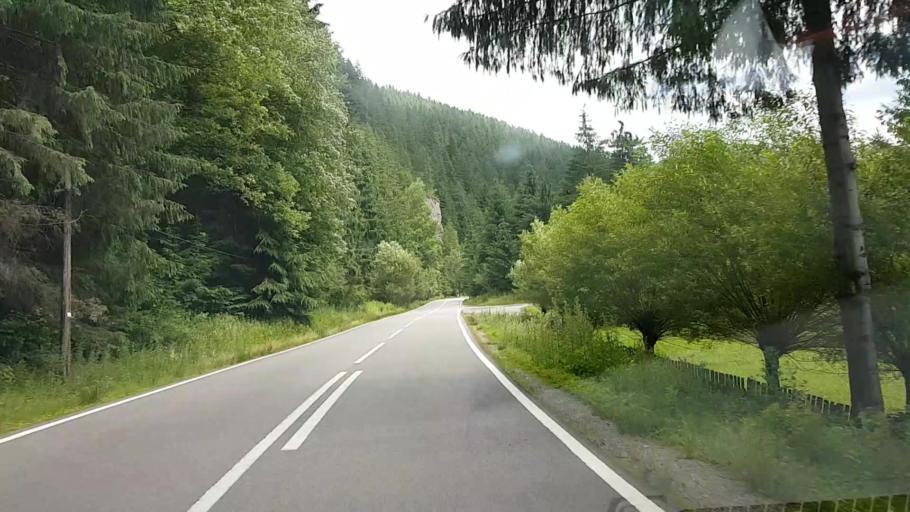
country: RO
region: Suceava
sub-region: Comuna Crucea
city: Crucea
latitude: 47.3627
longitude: 25.5967
